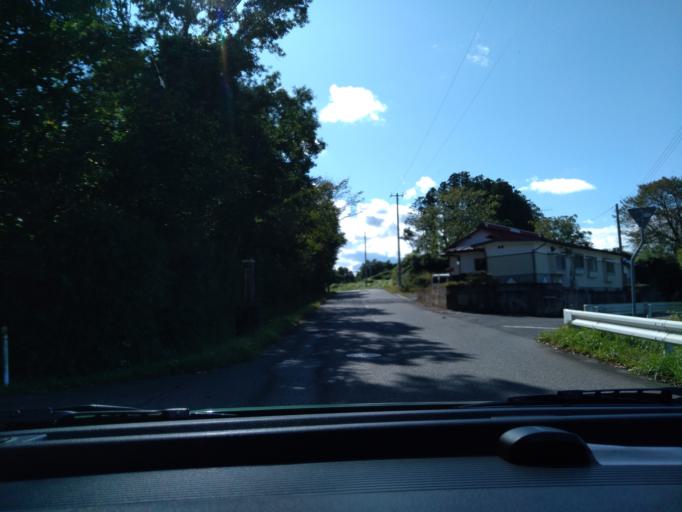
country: JP
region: Iwate
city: Ichinoseki
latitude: 38.7838
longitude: 141.2072
